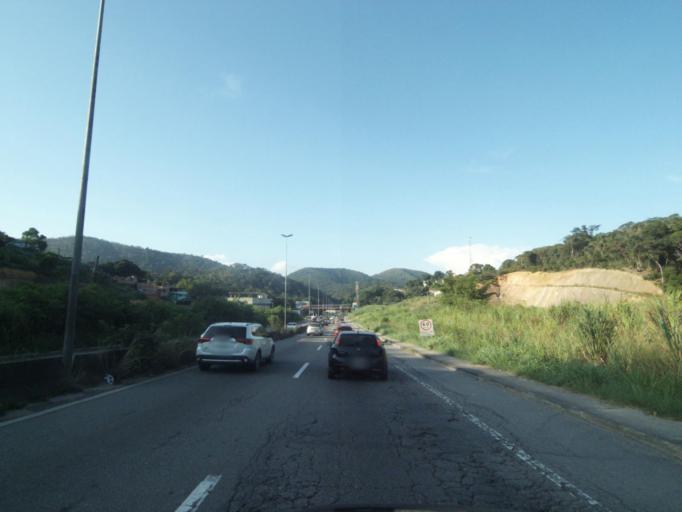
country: BR
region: Rio de Janeiro
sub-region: Niteroi
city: Niteroi
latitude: -22.8794
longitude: -43.0563
